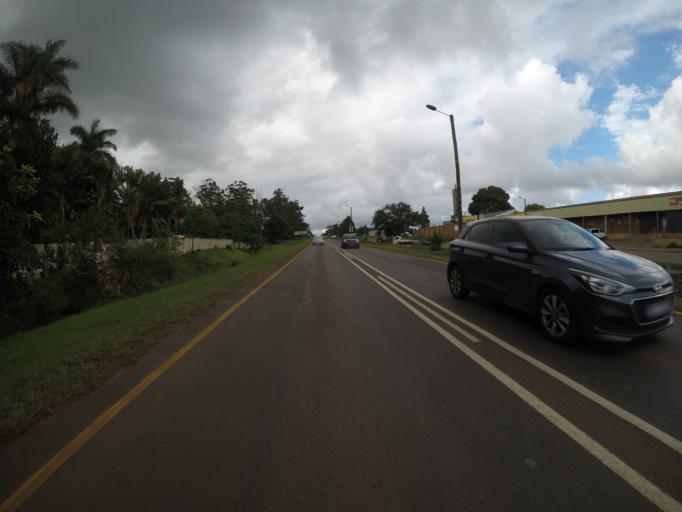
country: ZA
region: KwaZulu-Natal
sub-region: uMkhanyakude District Municipality
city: Mtubatuba
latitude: -28.4123
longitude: 32.1841
